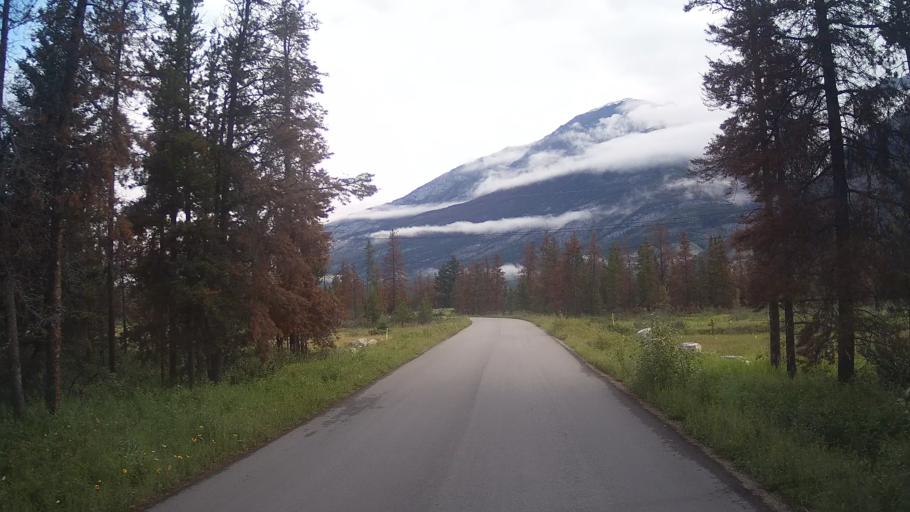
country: CA
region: Alberta
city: Jasper Park Lodge
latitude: 52.9669
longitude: -118.0599
